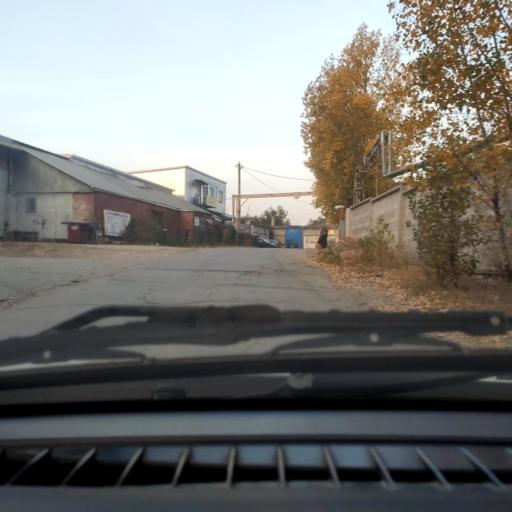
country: RU
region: Samara
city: Zhigulevsk
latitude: 53.4845
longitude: 49.4934
